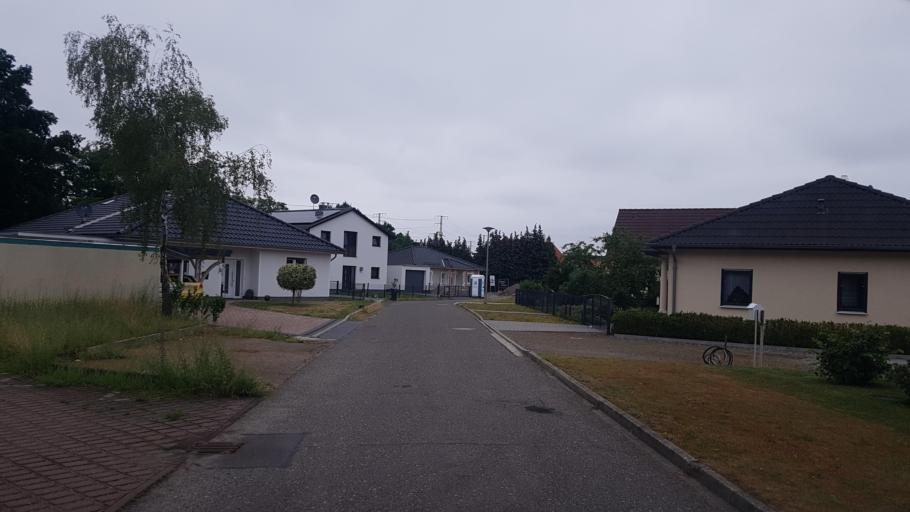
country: DE
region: Brandenburg
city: Senftenberg
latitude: 51.5219
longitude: 13.9959
